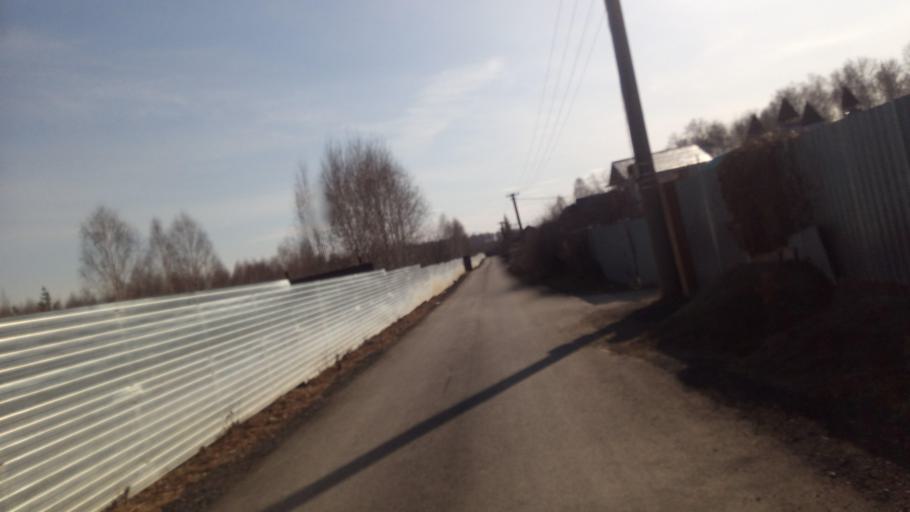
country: RU
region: Chelyabinsk
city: Sargazy
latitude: 55.1231
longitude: 61.2446
